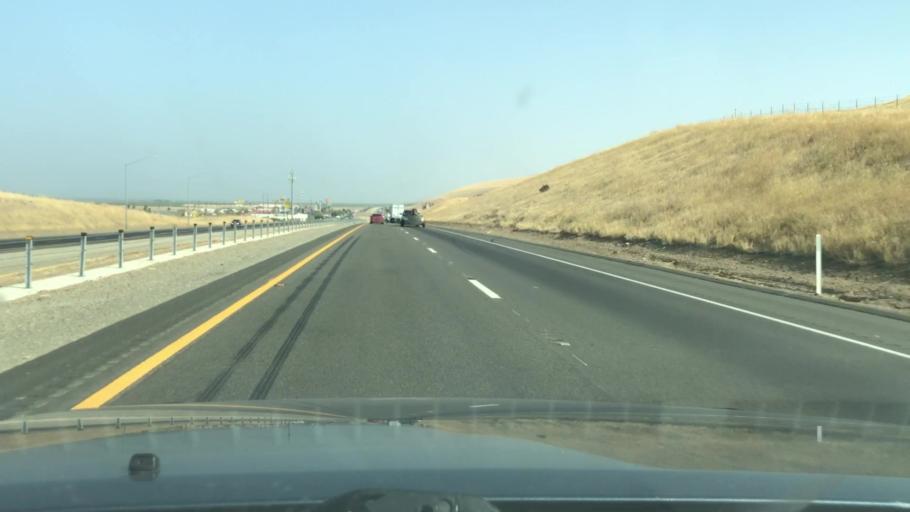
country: US
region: California
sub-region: Stanislaus County
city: Patterson
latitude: 37.5471
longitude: -121.2770
